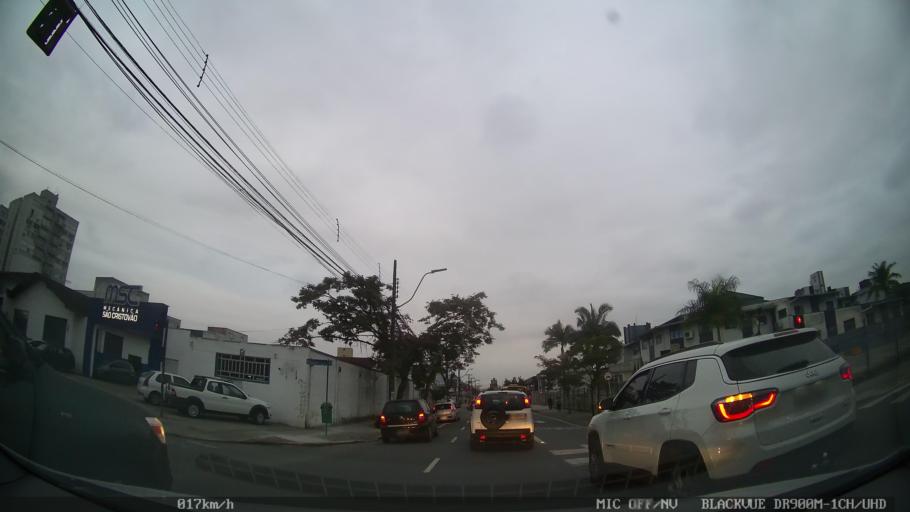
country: BR
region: Santa Catarina
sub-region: Joinville
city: Joinville
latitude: -26.2824
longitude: -48.8503
